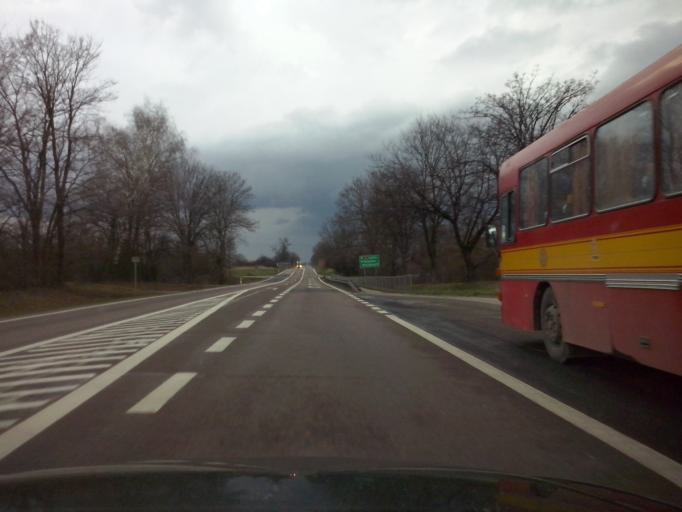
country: PL
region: Lublin Voivodeship
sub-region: Powiat chelmski
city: Rejowiec Fabryczny
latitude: 51.1741
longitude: 23.2689
